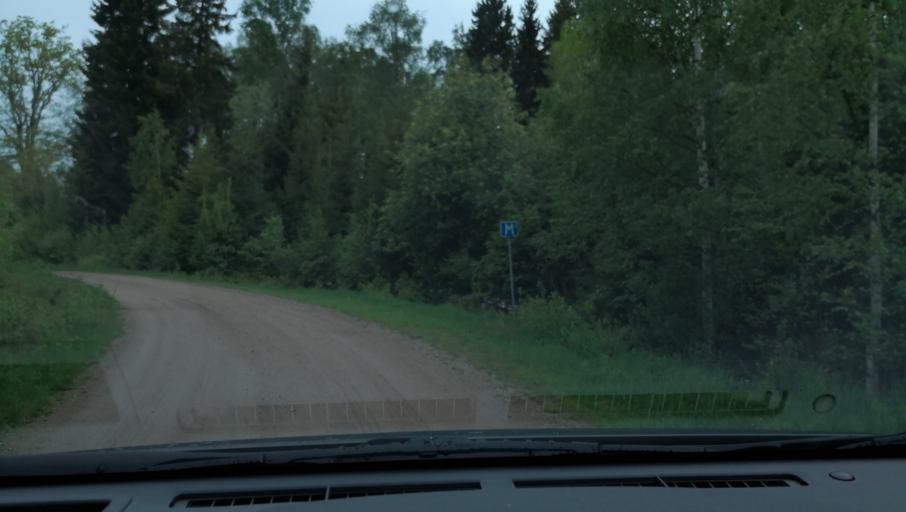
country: SE
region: Uppsala
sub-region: Enkopings Kommun
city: Orsundsbro
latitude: 59.9191
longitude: 17.3462
